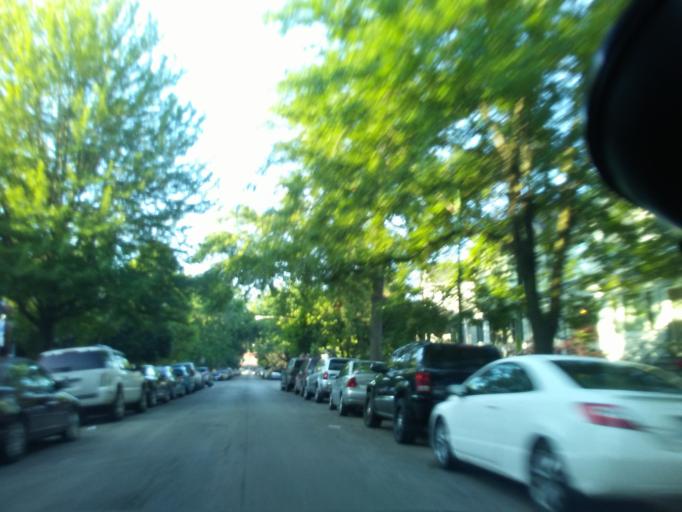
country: US
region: Illinois
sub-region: Cook County
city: Lincolnwood
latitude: 41.9270
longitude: -87.7158
